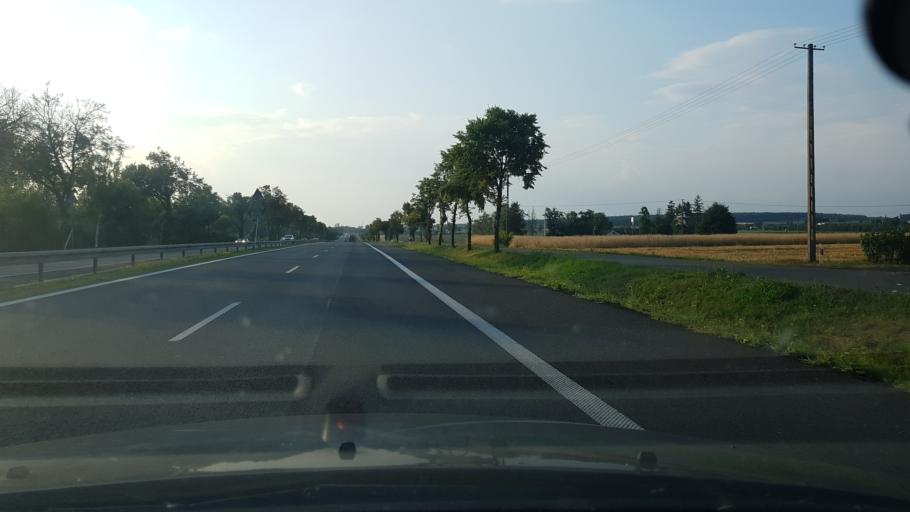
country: PL
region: Masovian Voivodeship
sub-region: Powiat plonski
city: Zaluski
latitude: 52.4891
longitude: 20.5473
